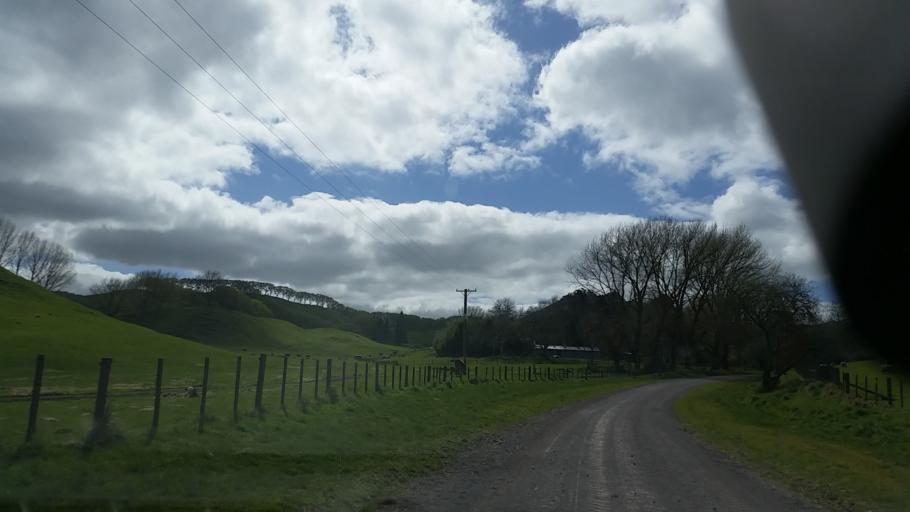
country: NZ
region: Bay of Plenty
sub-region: Rotorua District
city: Rotorua
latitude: -38.3113
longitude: 176.3028
